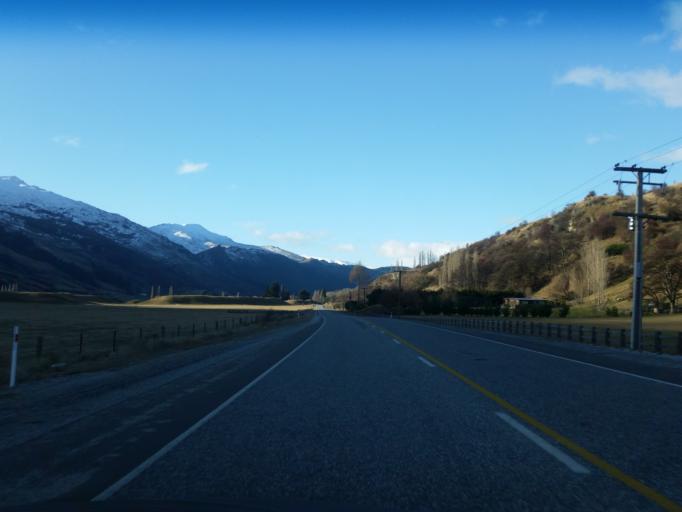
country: NZ
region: Otago
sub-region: Queenstown-Lakes District
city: Queenstown
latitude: -44.9669
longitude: 168.7086
